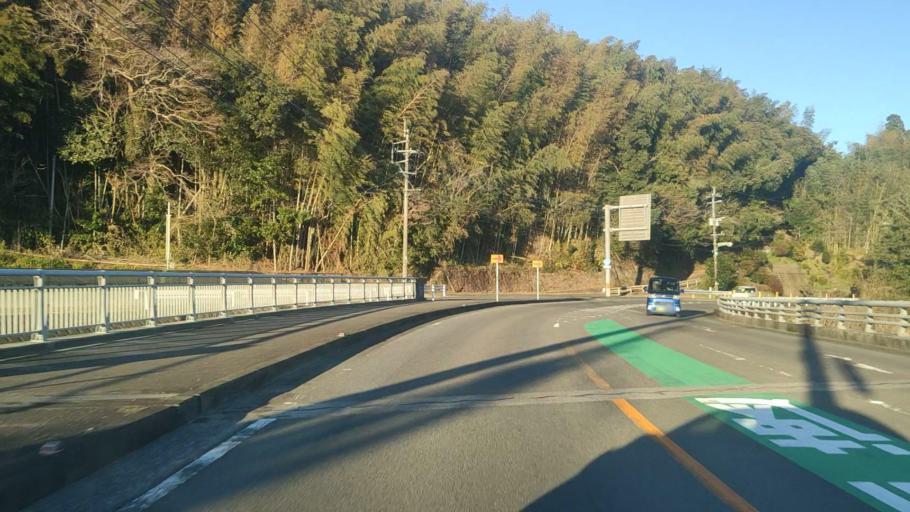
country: JP
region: Miyazaki
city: Miyazaki-shi
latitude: 31.8591
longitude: 131.3686
